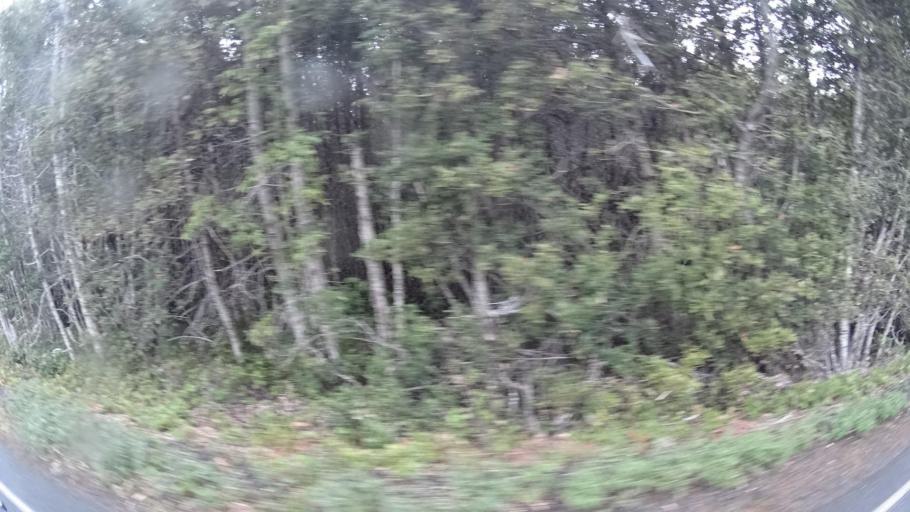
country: US
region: California
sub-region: Humboldt County
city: Willow Creek
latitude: 41.1872
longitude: -123.8159
